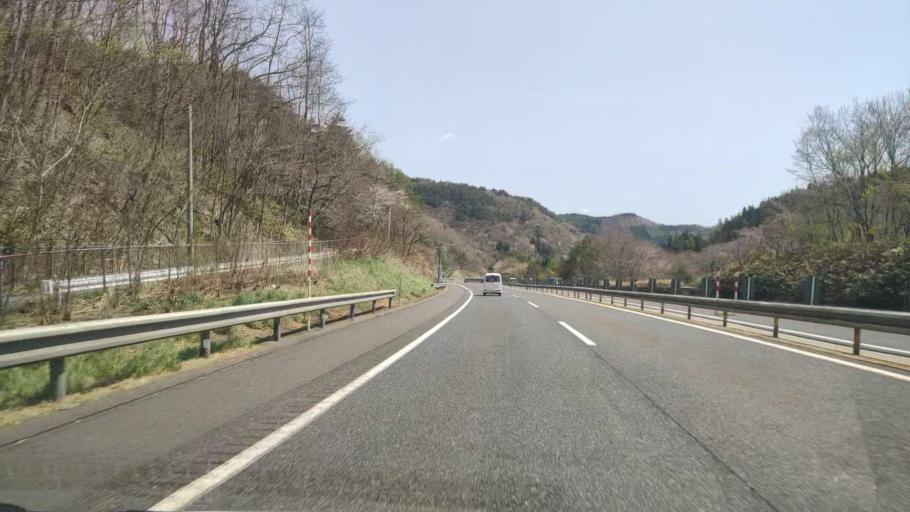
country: JP
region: Iwate
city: Ichinohe
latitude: 40.2199
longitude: 141.2474
